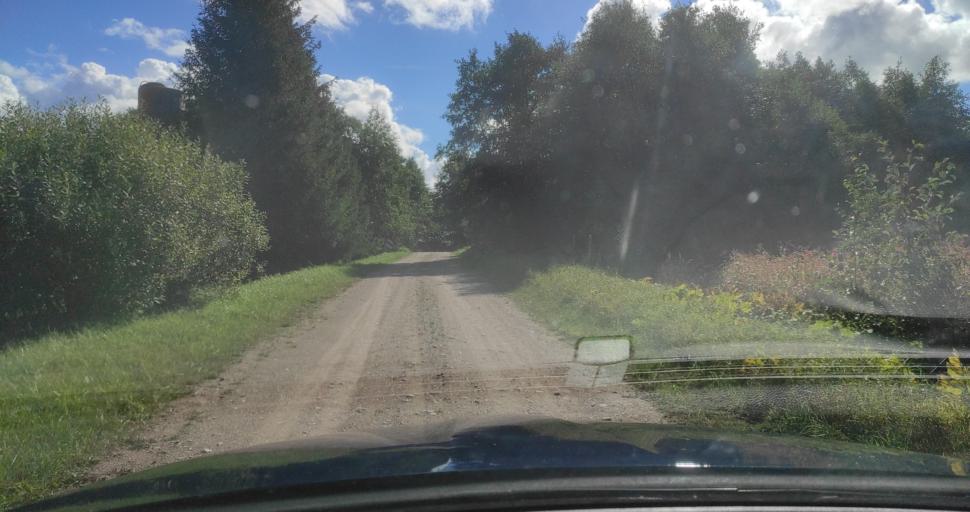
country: LV
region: Ventspils
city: Ventspils
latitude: 57.3695
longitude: 21.6313
